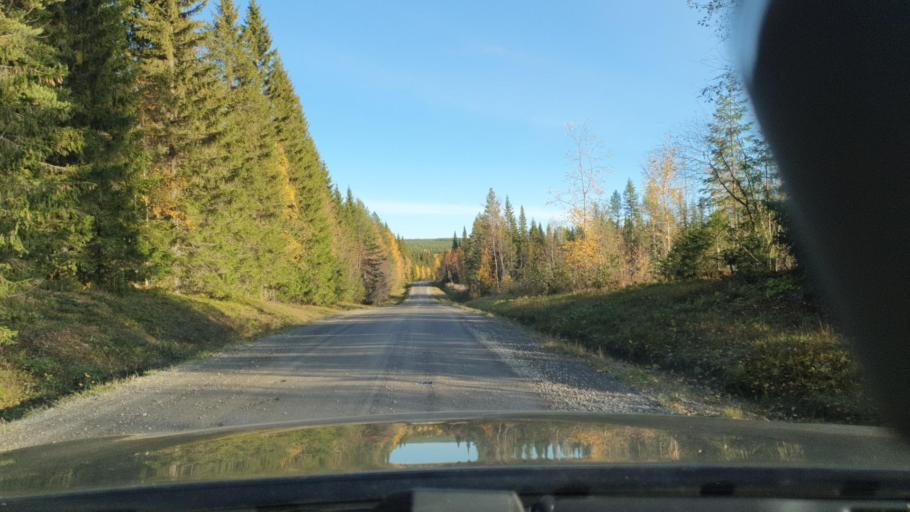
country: SE
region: Jaemtland
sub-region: Stroemsunds Kommun
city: Stroemsund
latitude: 63.5162
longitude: 15.6458
